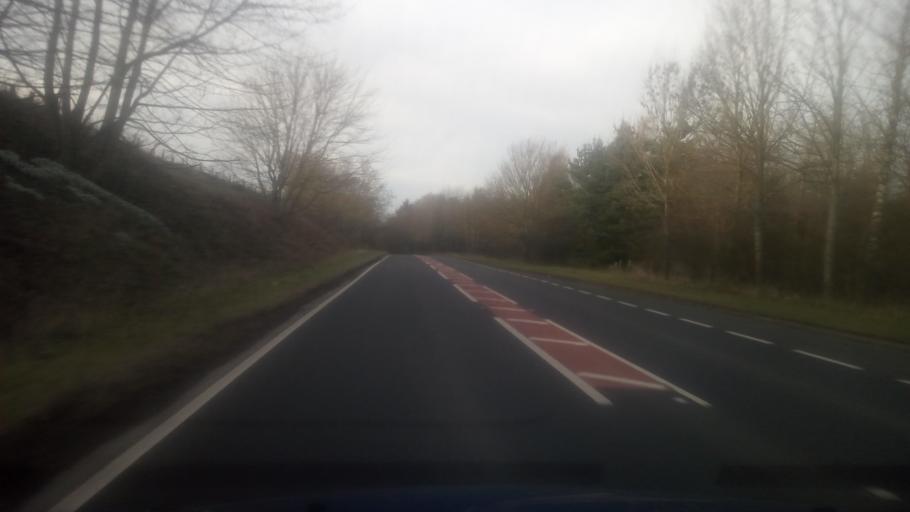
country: GB
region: Scotland
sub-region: The Scottish Borders
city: Jedburgh
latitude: 55.4372
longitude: -2.5430
